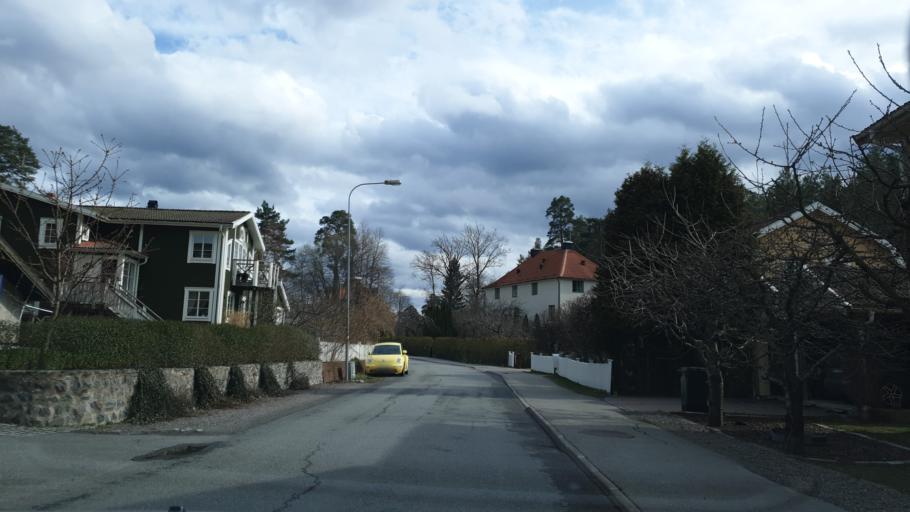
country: SE
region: Stockholm
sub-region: Nacka Kommun
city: Saltsjobaden
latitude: 59.2698
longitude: 18.3088
